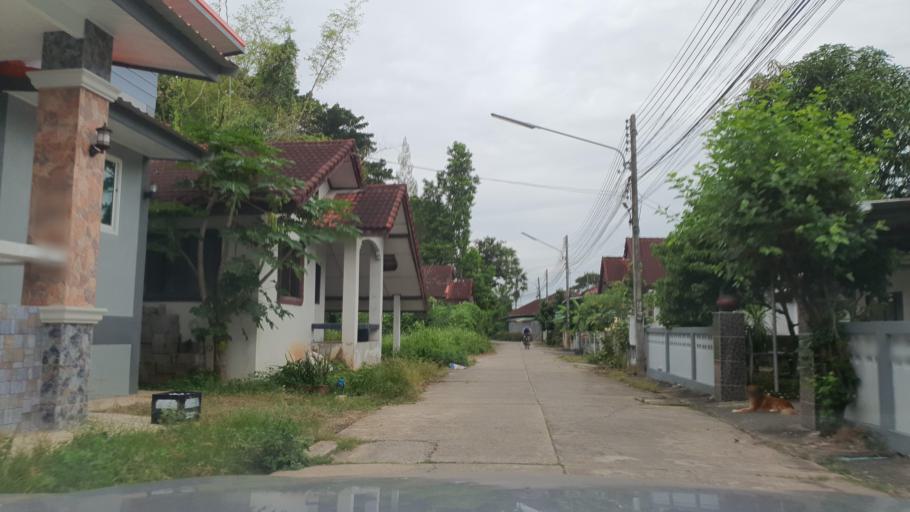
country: TH
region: Chiang Mai
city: San Sai
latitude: 18.9337
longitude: 98.9324
